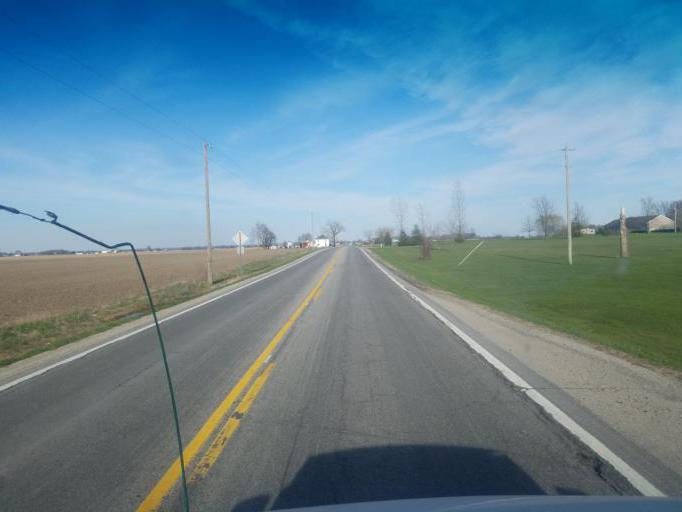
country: US
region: Ohio
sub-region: Logan County
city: De Graff
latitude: 40.3362
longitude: -84.0170
